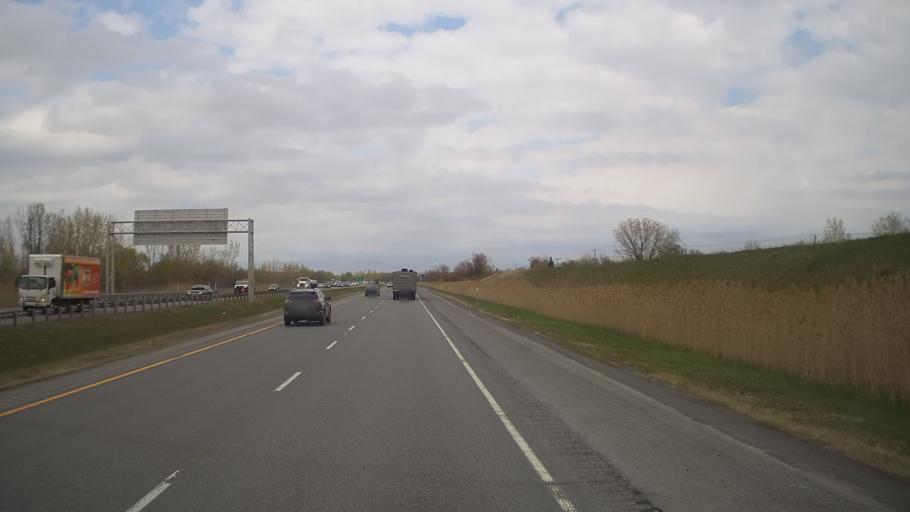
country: CA
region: Quebec
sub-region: Monteregie
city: Candiac
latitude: 45.3835
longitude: -73.4799
